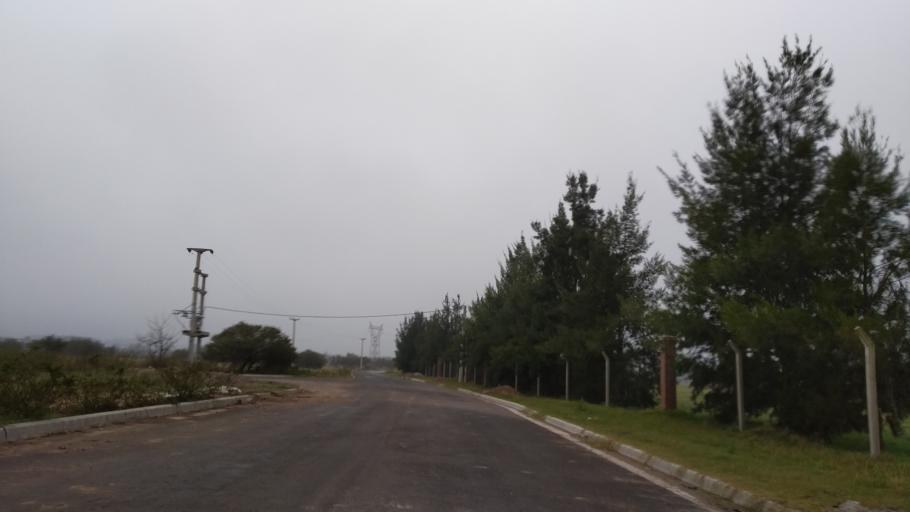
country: AR
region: Santa Fe
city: Funes
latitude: -32.9376
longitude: -60.7681
